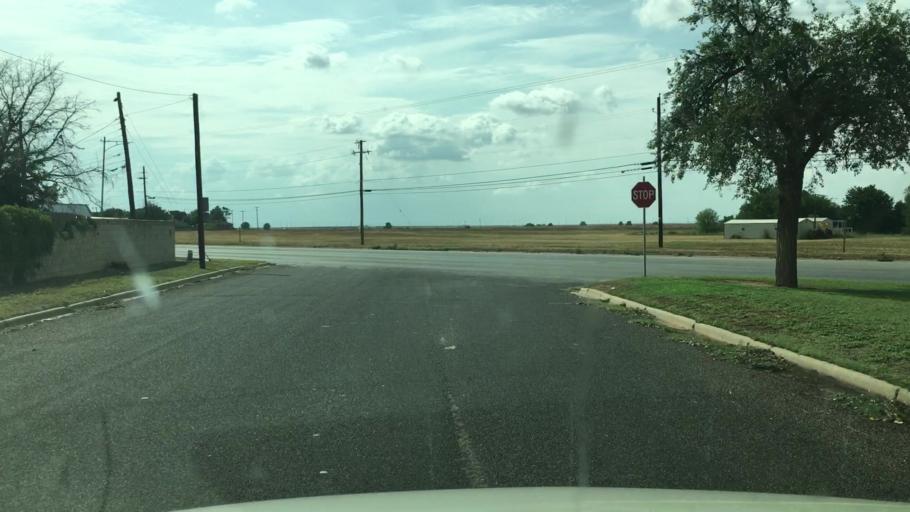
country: US
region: Texas
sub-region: Dawson County
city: Lamesa
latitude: 32.7533
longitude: -101.9565
